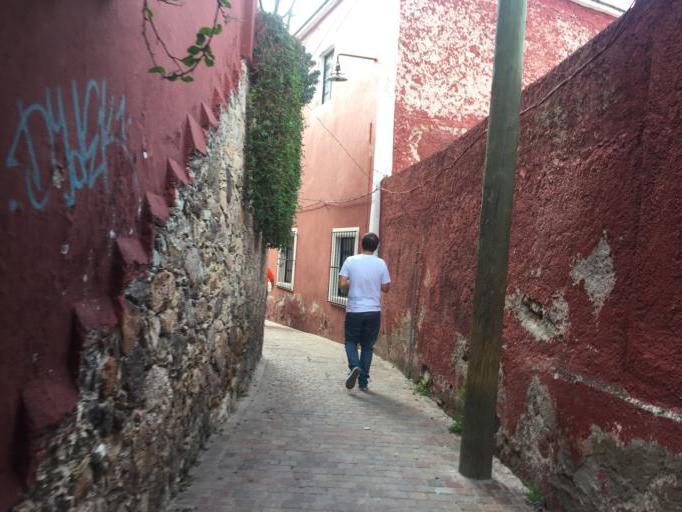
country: MX
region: Guanajuato
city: Guanajuato
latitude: 21.0155
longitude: -101.2548
